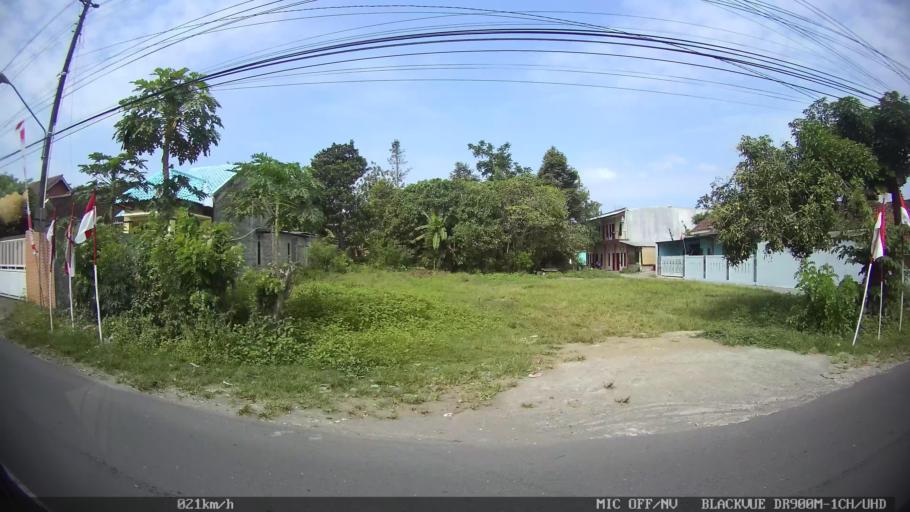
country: ID
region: Daerah Istimewa Yogyakarta
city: Depok
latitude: -7.7723
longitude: 110.4376
